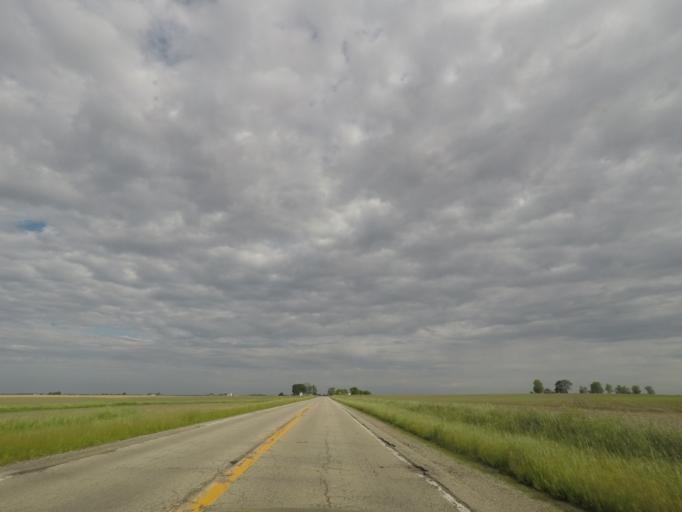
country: US
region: Illinois
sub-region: Logan County
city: Mount Pulaski
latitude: 40.0722
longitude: -89.2932
